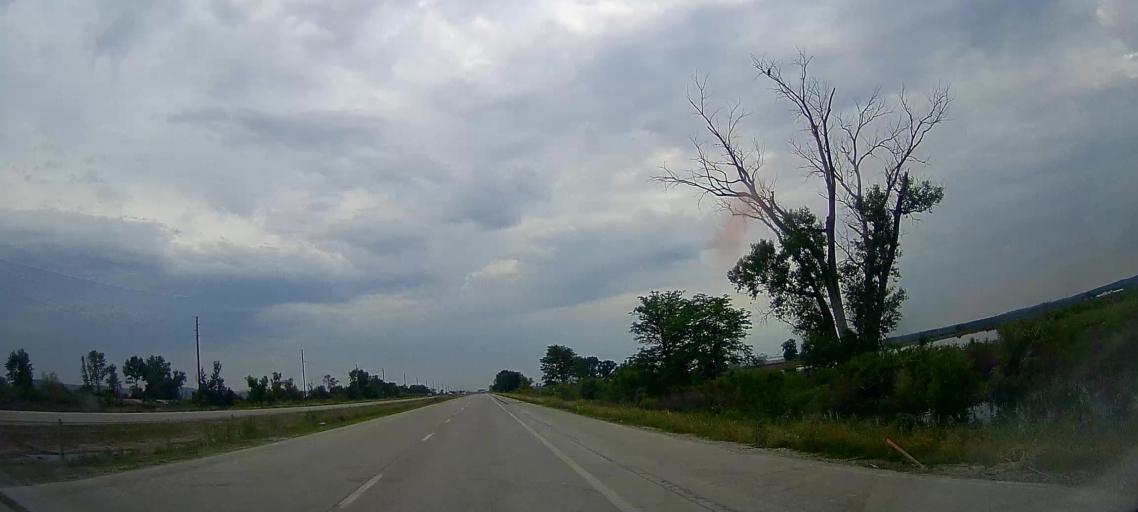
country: US
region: Iowa
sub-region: Pottawattamie County
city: Carter Lake
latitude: 41.3983
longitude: -95.8997
